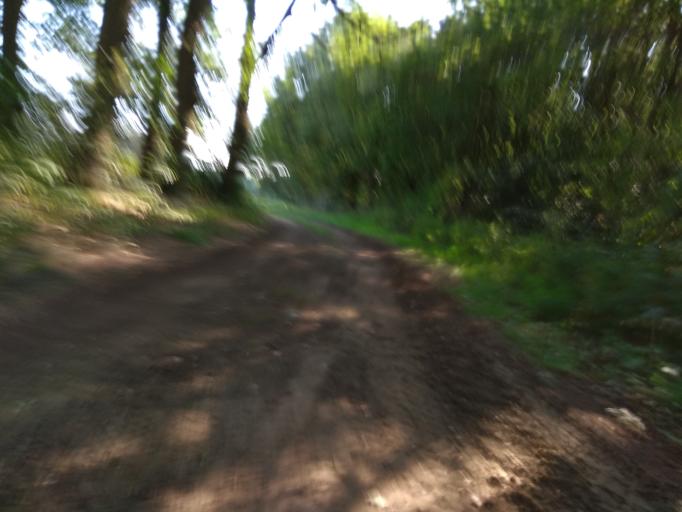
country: DE
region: North Rhine-Westphalia
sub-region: Regierungsbezirk Munster
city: Klein Reken
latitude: 51.7452
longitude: 7.0361
